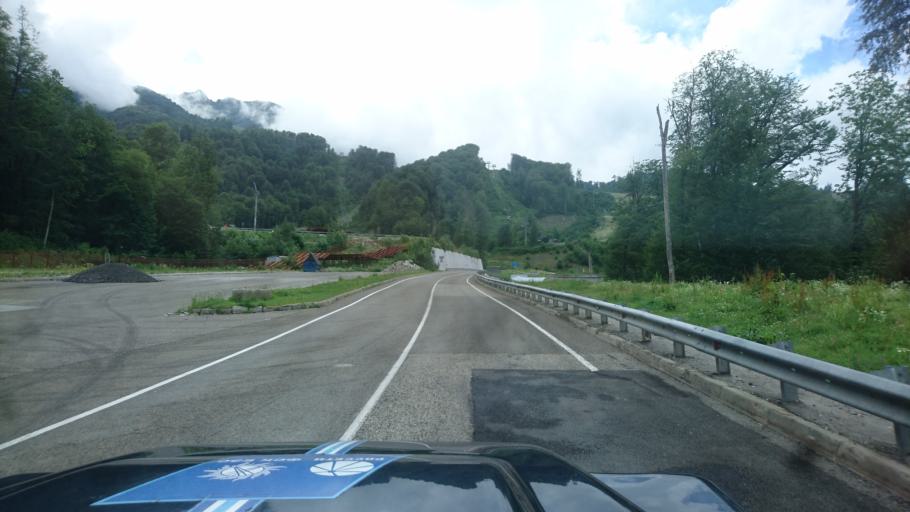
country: RU
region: Krasnodarskiy
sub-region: Sochi City
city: Krasnaya Polyana
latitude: 43.6488
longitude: 40.3366
